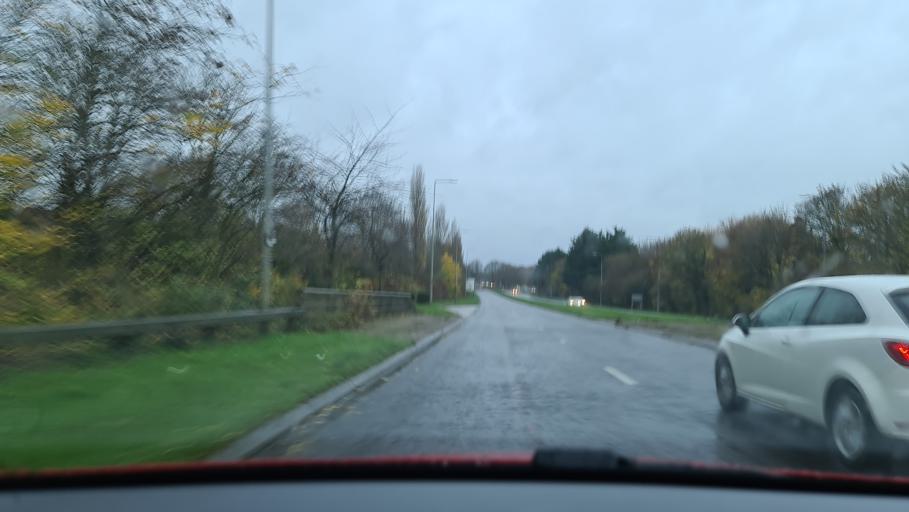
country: GB
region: England
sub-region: Milton Keynes
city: Bradwell
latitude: 52.0552
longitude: -0.7804
